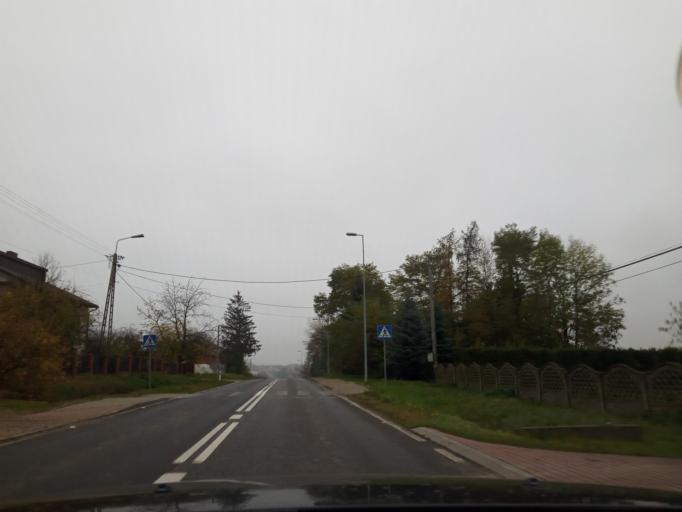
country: PL
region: Lesser Poland Voivodeship
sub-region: Powiat proszowicki
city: Klimontow
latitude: 50.2281
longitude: 20.3316
